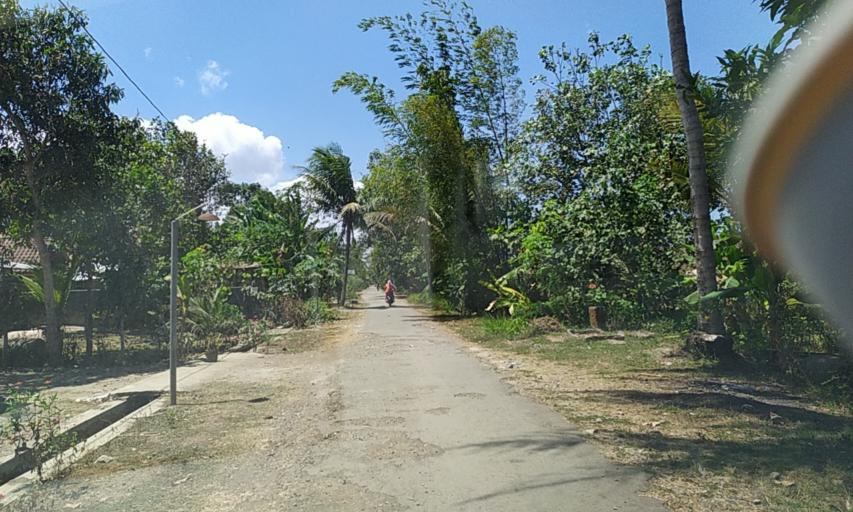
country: ID
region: Central Java
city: Mernek
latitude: -7.6227
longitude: 109.1746
